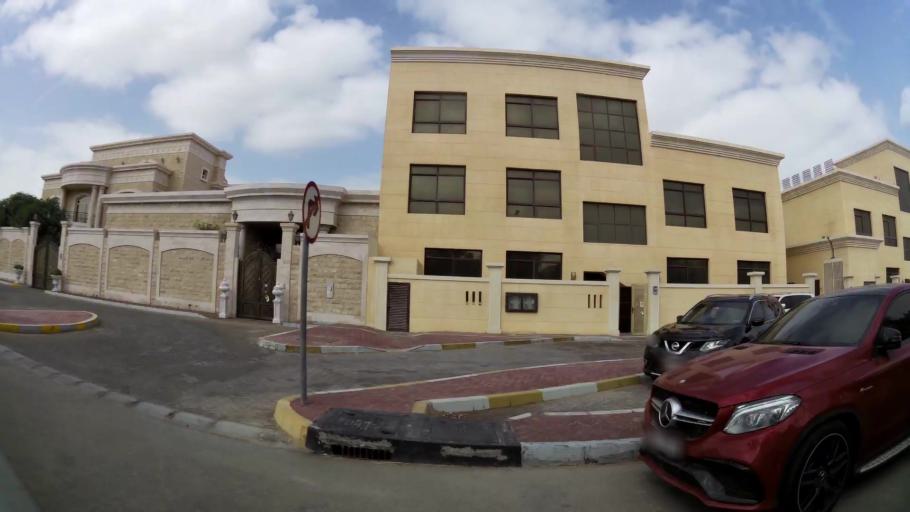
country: AE
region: Abu Dhabi
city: Abu Dhabi
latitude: 24.4111
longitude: 54.4966
